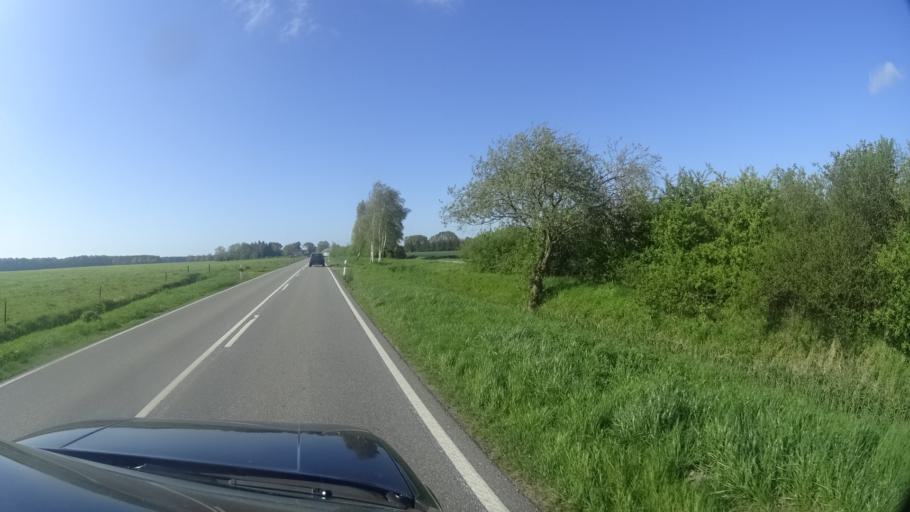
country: DE
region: Mecklenburg-Vorpommern
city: Ostseebad Dierhagen
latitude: 54.2550
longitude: 12.3570
